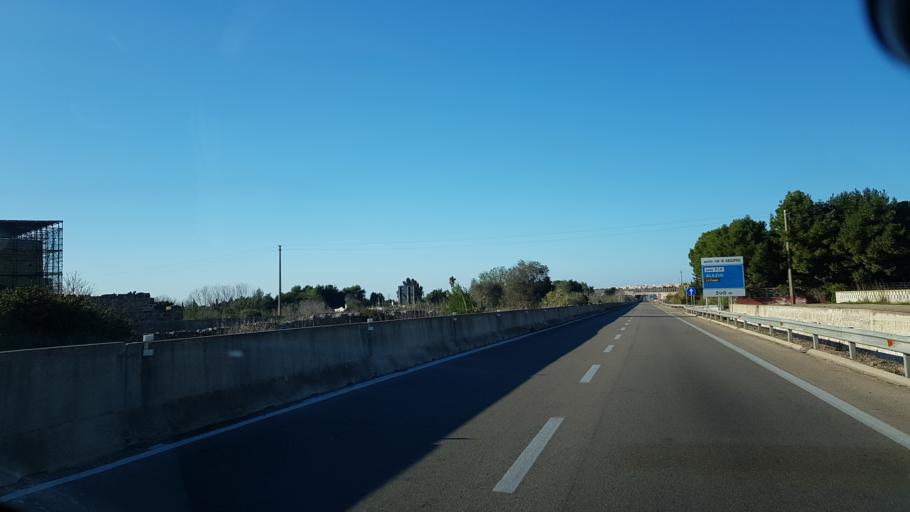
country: IT
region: Apulia
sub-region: Provincia di Lecce
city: Alezio
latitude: 40.0280
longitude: 18.0342
